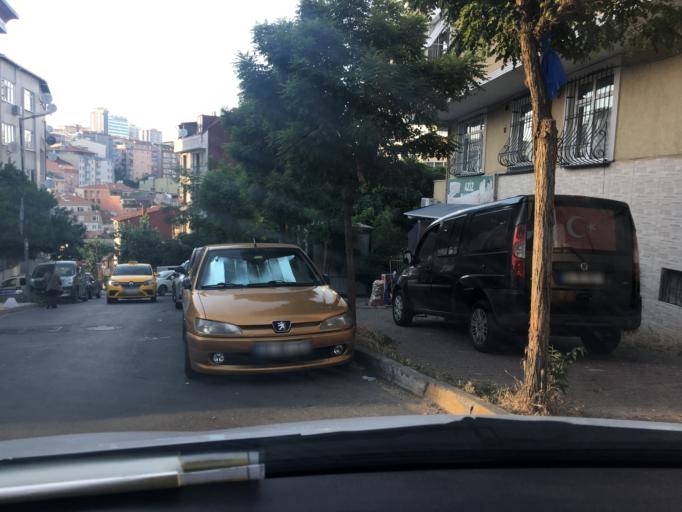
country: TR
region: Istanbul
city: Sisli
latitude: 41.0556
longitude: 28.9744
